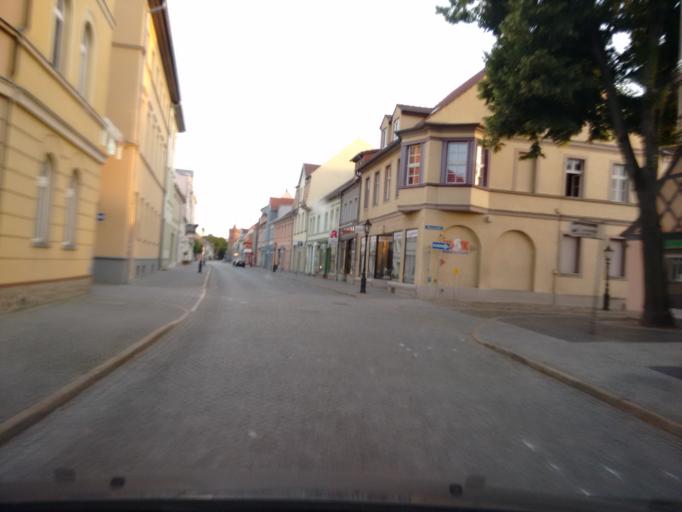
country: DE
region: Brandenburg
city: Beeskow
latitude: 52.1737
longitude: 14.2477
